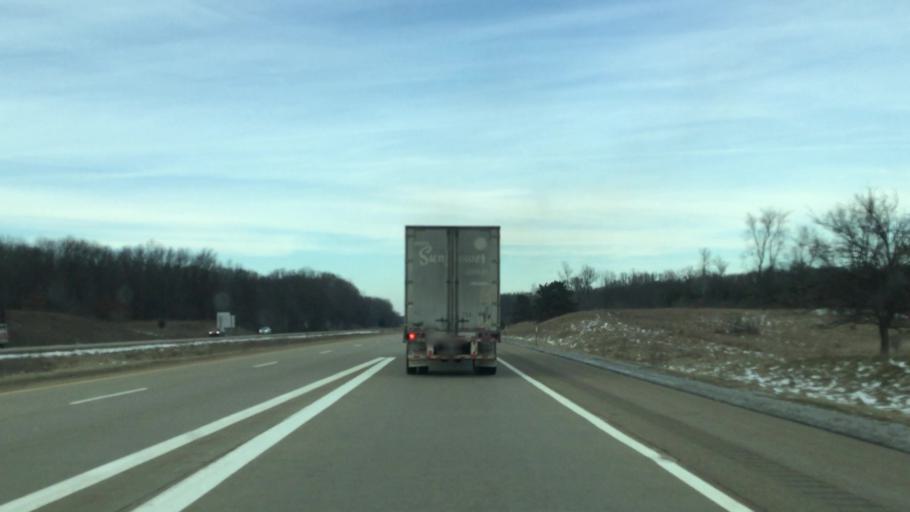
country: US
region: Michigan
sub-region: Calhoun County
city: Marshall
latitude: 42.3046
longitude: -84.9952
